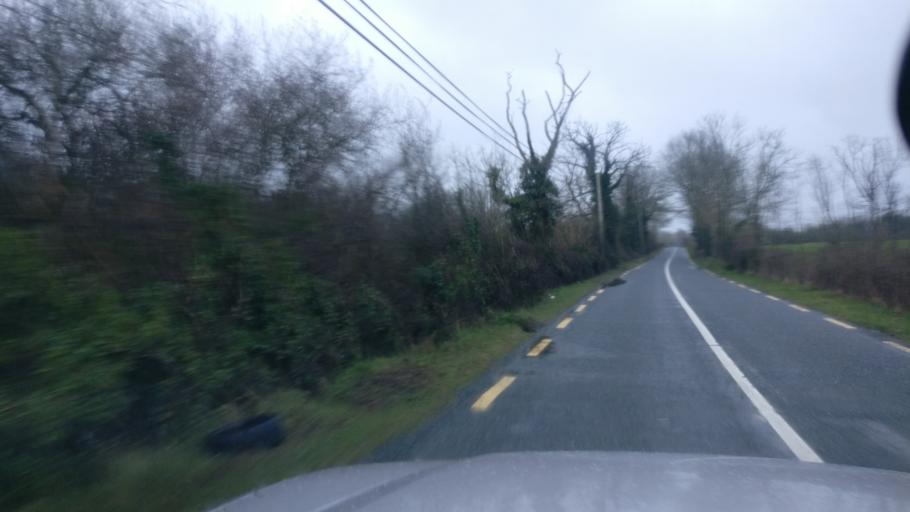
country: IE
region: Connaught
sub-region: County Galway
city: Ballinasloe
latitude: 53.2293
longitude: -8.1904
